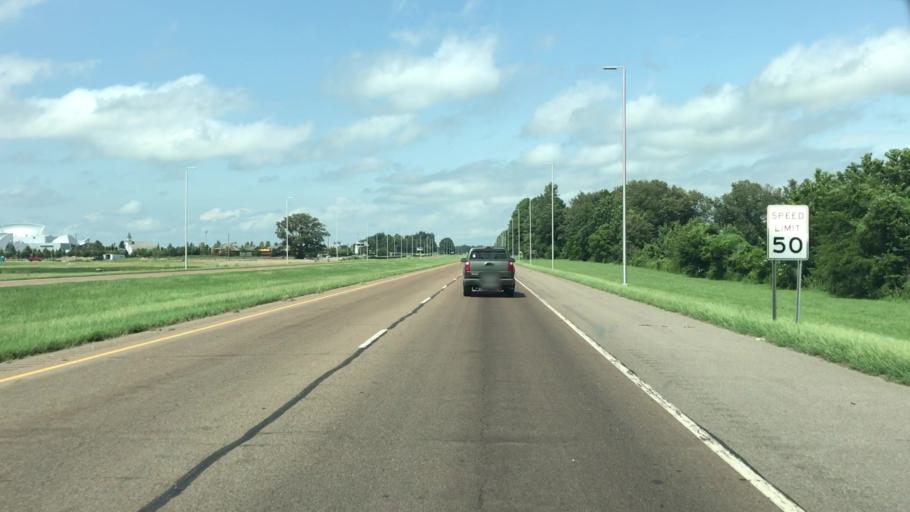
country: US
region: Tennessee
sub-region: Obion County
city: Union City
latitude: 36.4321
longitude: -89.0671
